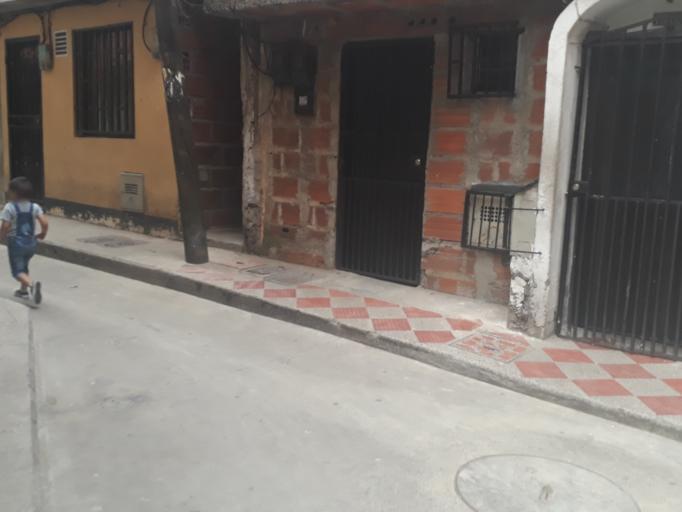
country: CO
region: Antioquia
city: Medellin
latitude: 6.2744
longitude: -75.5658
